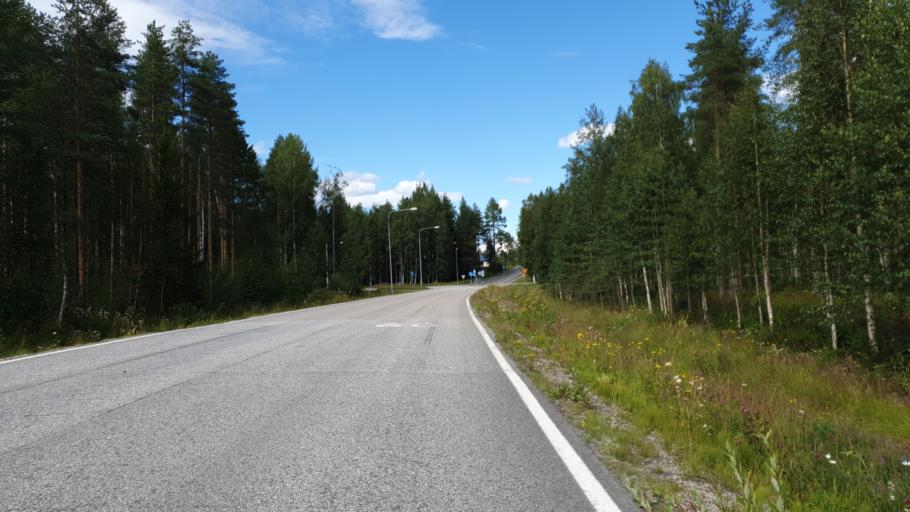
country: FI
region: Kainuu
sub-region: Kehys-Kainuu
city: Kuhmo
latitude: 64.1174
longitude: 29.5269
